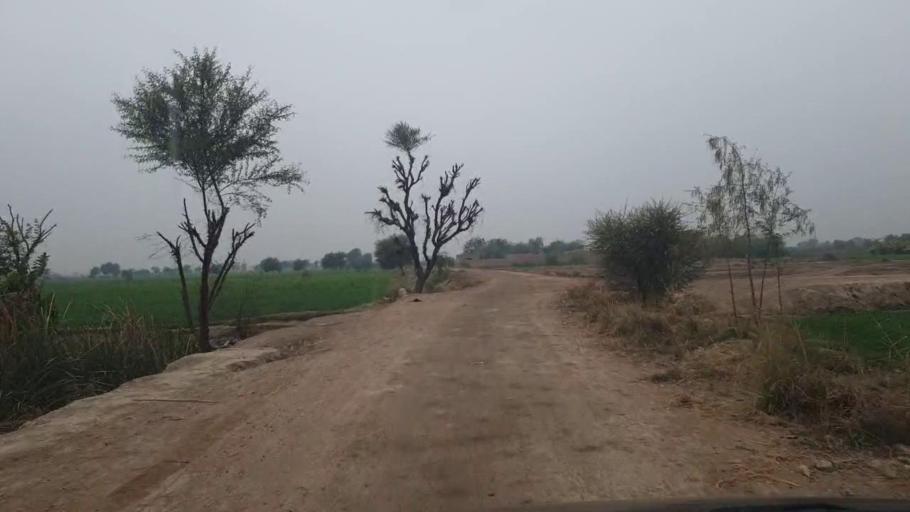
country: PK
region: Sindh
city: Tando Adam
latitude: 25.8289
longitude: 68.6789
